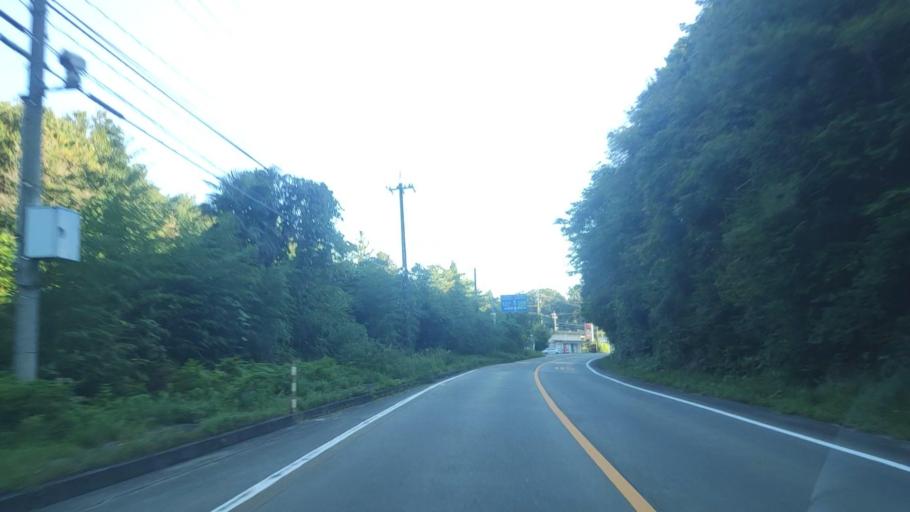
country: JP
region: Ishikawa
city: Nanao
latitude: 37.1328
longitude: 136.8635
